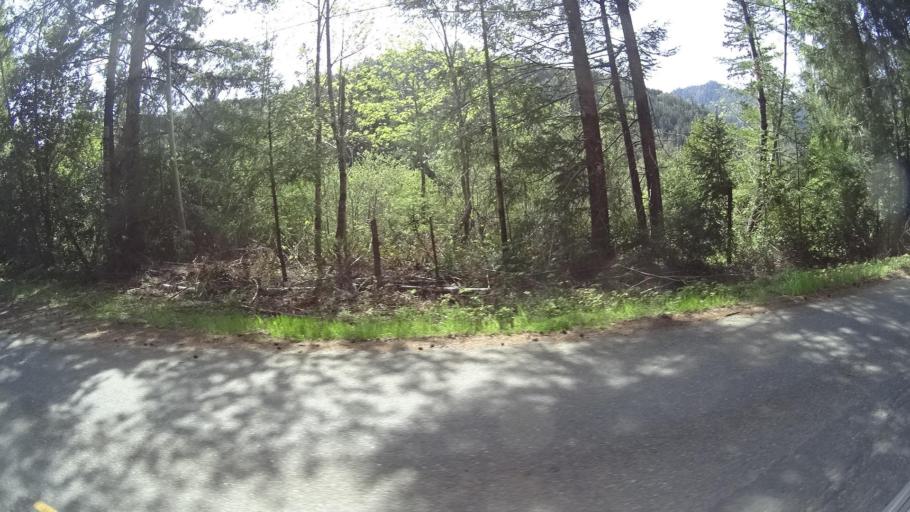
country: US
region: California
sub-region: Humboldt County
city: Redway
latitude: 40.3769
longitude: -123.7422
